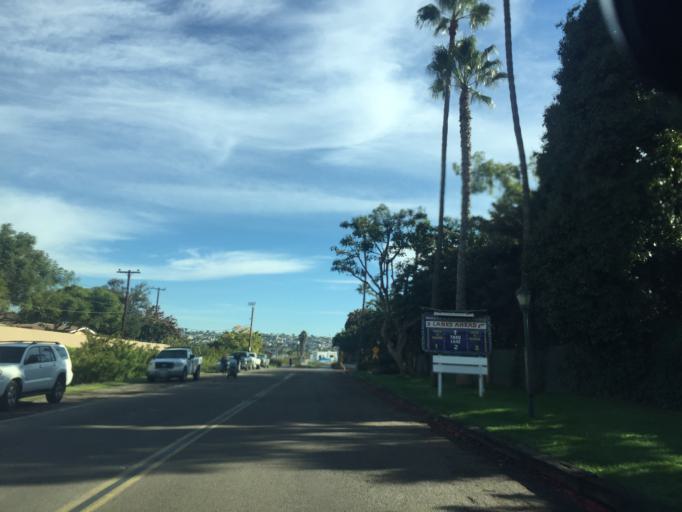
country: US
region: California
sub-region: San Diego County
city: La Jolla
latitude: 32.7969
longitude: -117.2266
